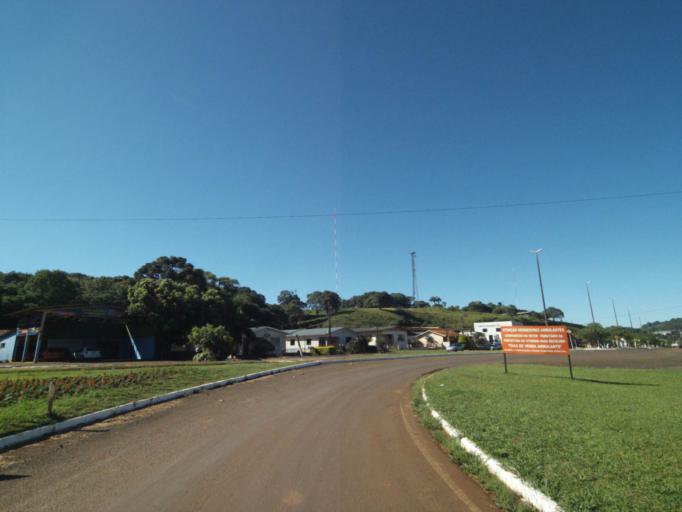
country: BR
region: Parana
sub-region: Pato Branco
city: Pato Branco
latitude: -26.2588
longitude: -52.7738
